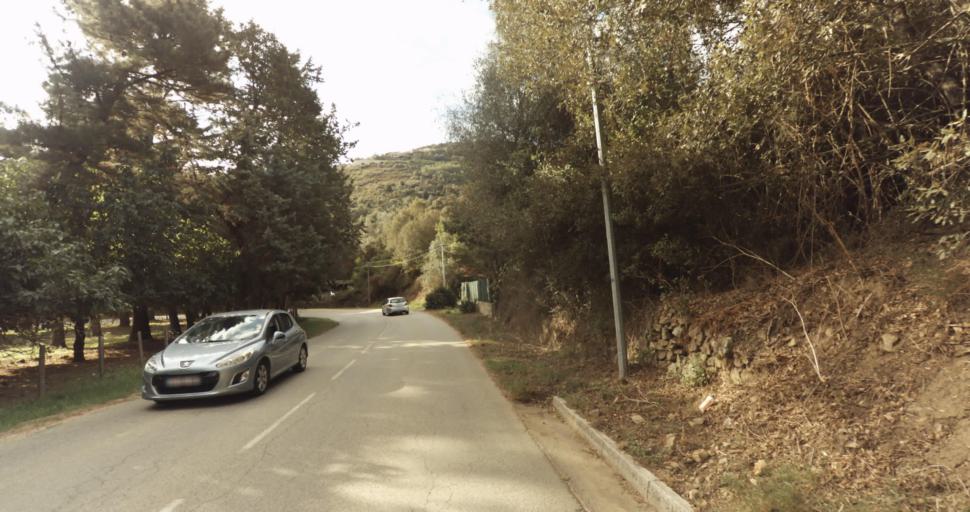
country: FR
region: Corsica
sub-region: Departement de la Corse-du-Sud
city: Ajaccio
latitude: 41.9301
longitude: 8.7123
